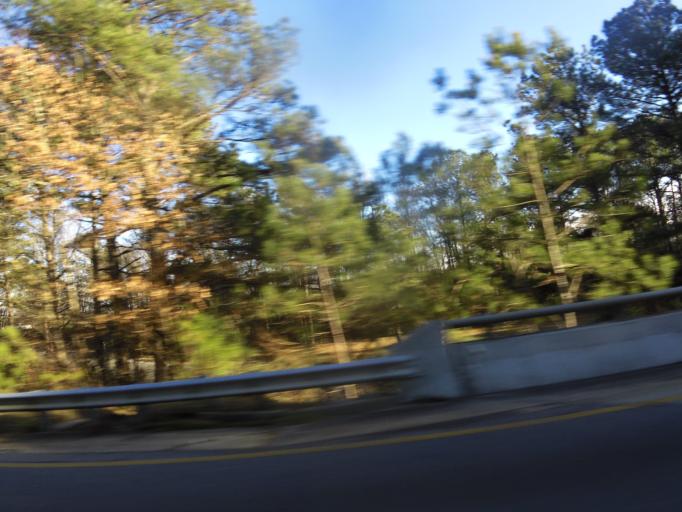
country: US
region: Virginia
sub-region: Isle of Wight County
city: Windsor
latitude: 36.6841
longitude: -76.7711
